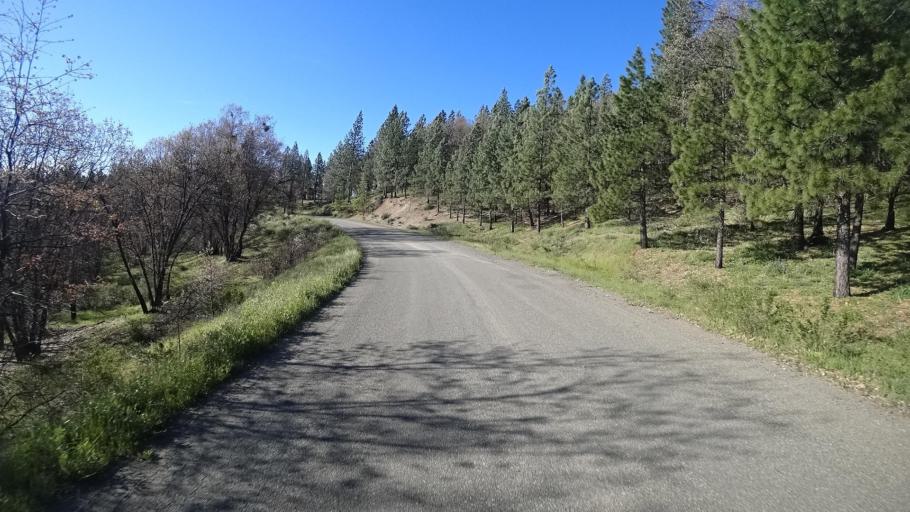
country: US
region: California
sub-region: Lake County
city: Upper Lake
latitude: 39.3141
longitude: -122.9468
